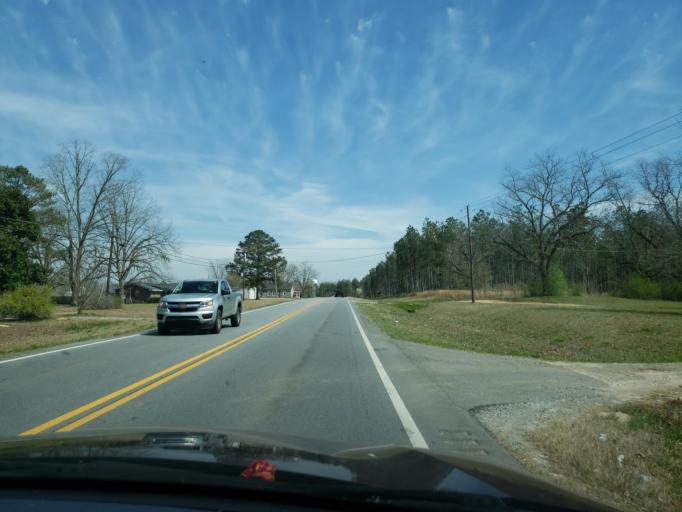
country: US
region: Alabama
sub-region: Elmore County
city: Tallassee
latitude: 32.5576
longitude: -85.8248
